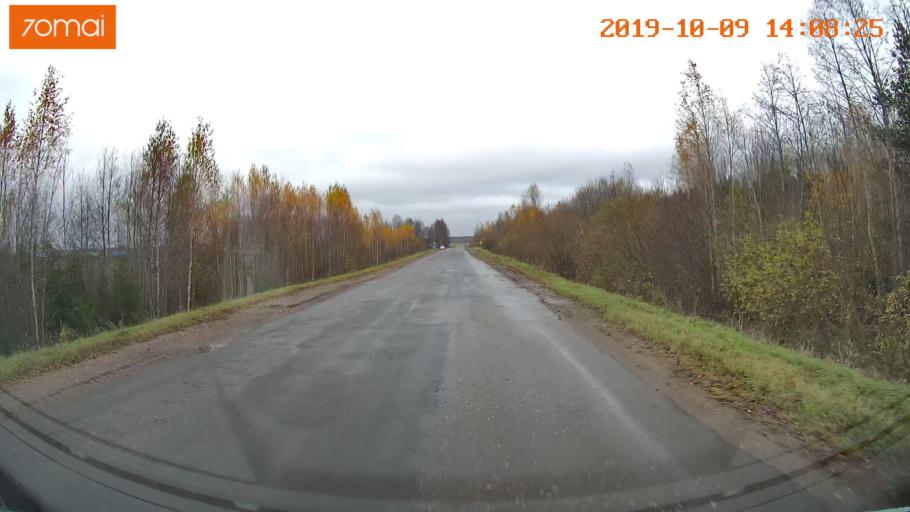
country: RU
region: Kostroma
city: Buy
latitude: 58.4766
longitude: 41.4357
